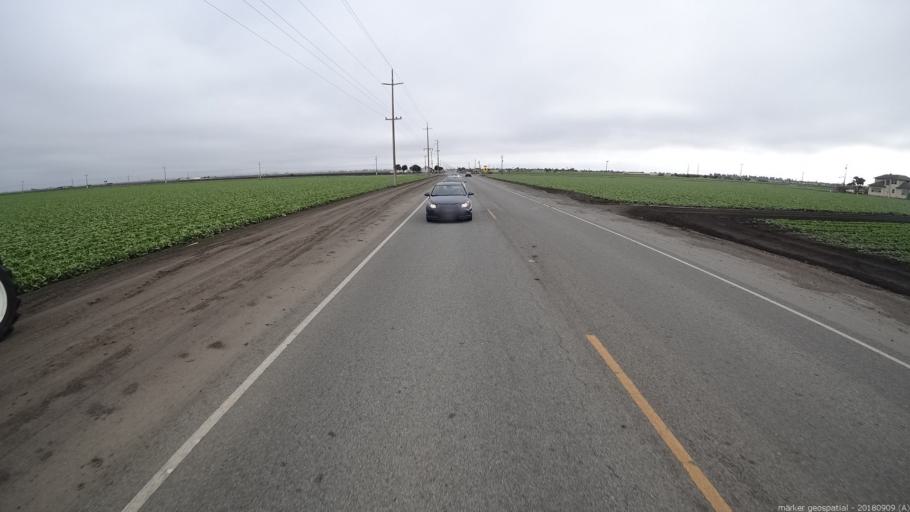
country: US
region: California
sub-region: Monterey County
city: Salinas
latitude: 36.6570
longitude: -121.6935
